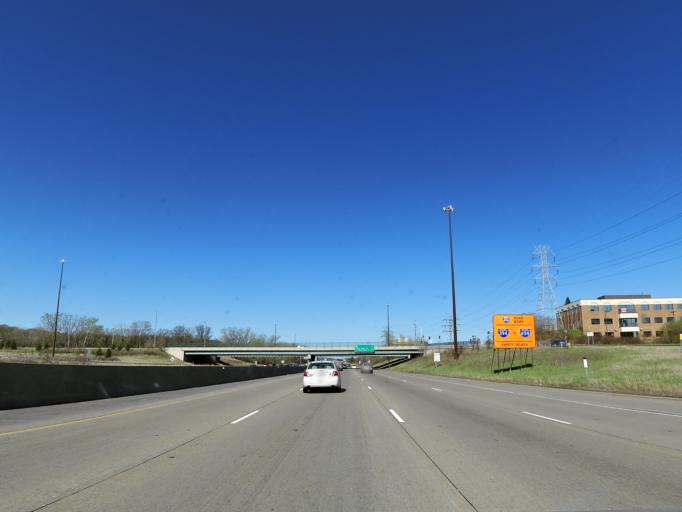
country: US
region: Minnesota
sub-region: Hennepin County
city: Edina
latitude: 44.8596
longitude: -93.3597
